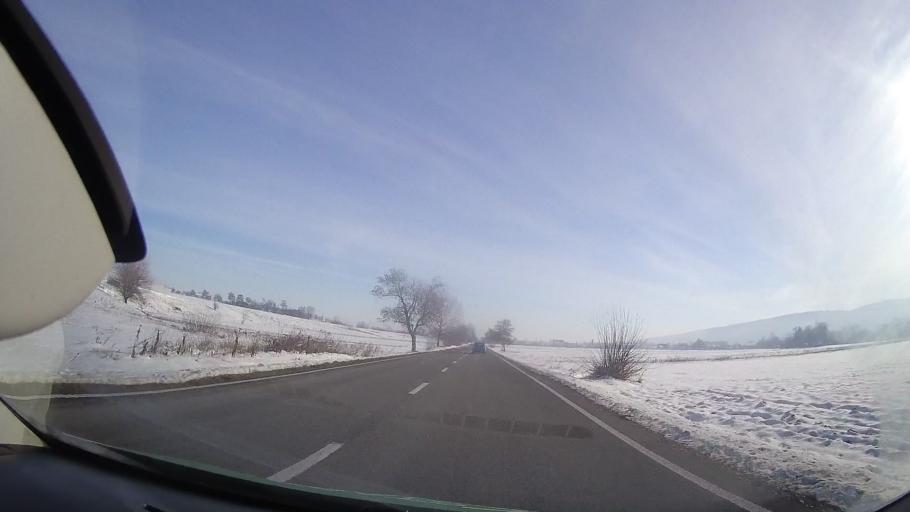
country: RO
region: Neamt
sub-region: Comuna Negresti
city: Negresti
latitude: 47.0656
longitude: 26.3744
